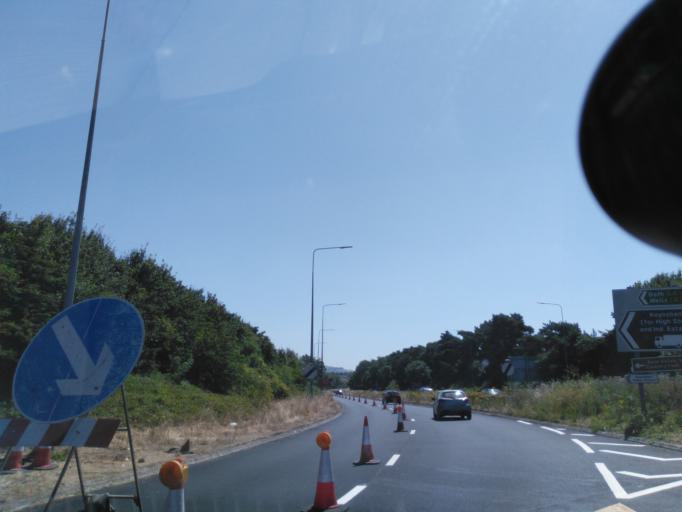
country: GB
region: England
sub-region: Bath and North East Somerset
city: Keynsham
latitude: 51.4254
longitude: -2.5162
